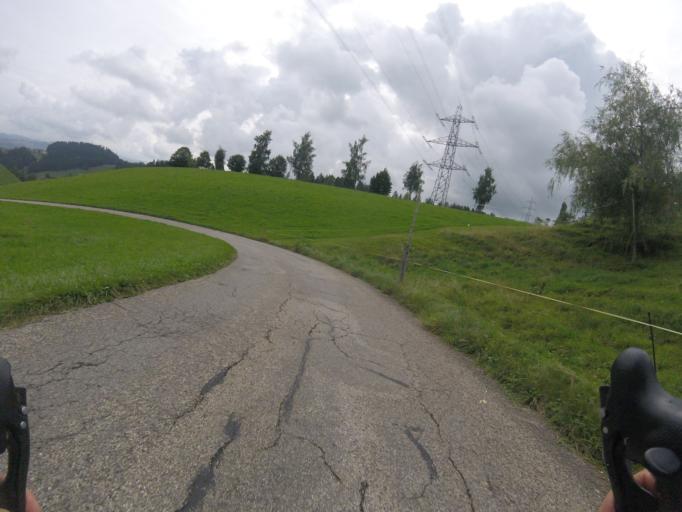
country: CH
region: Bern
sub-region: Emmental District
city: Lutzelfluh
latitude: 46.9756
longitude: 7.6785
